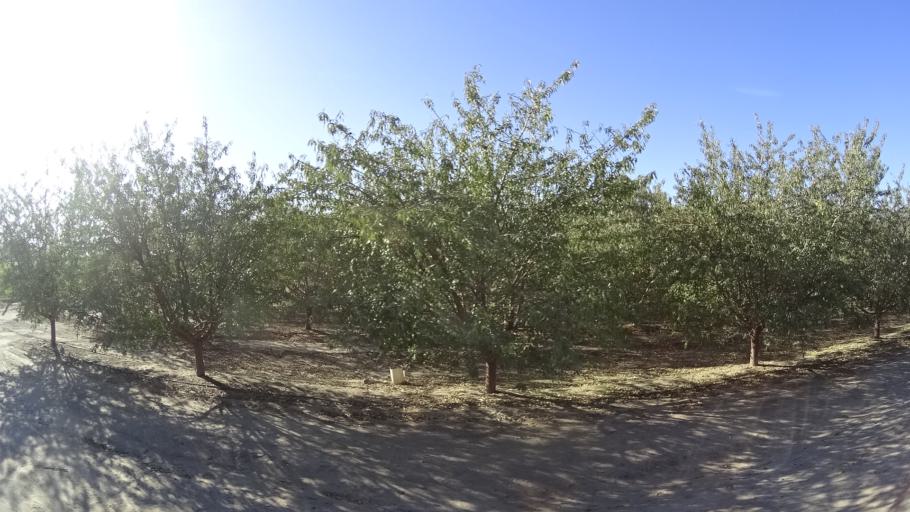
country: US
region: California
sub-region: Kern County
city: Greenacres
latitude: 35.2711
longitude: -119.1187
